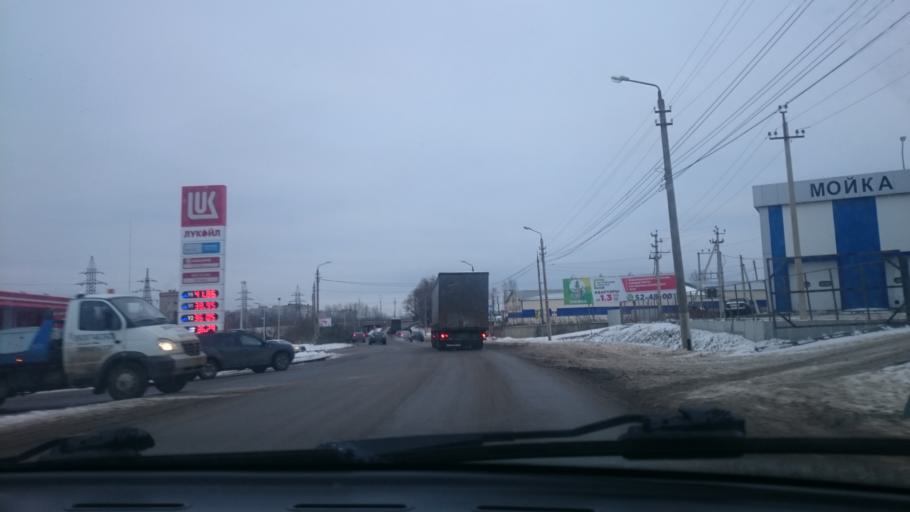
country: RU
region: Tula
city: Tula
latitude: 54.1691
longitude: 37.6346
